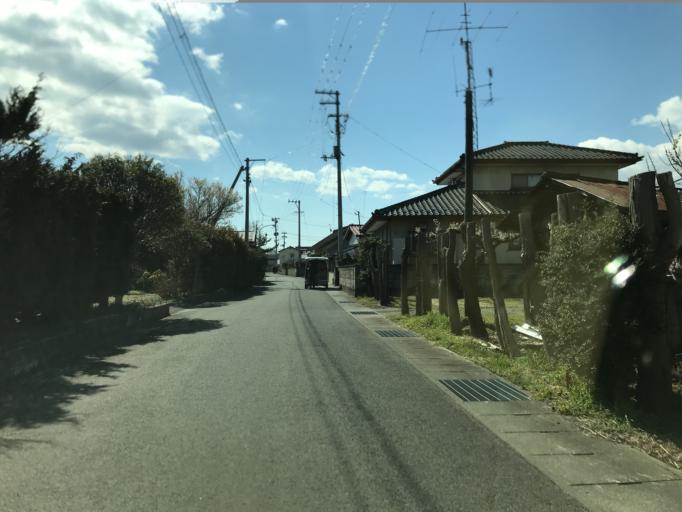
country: JP
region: Fukushima
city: Fukushima-shi
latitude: 37.7410
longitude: 140.4134
